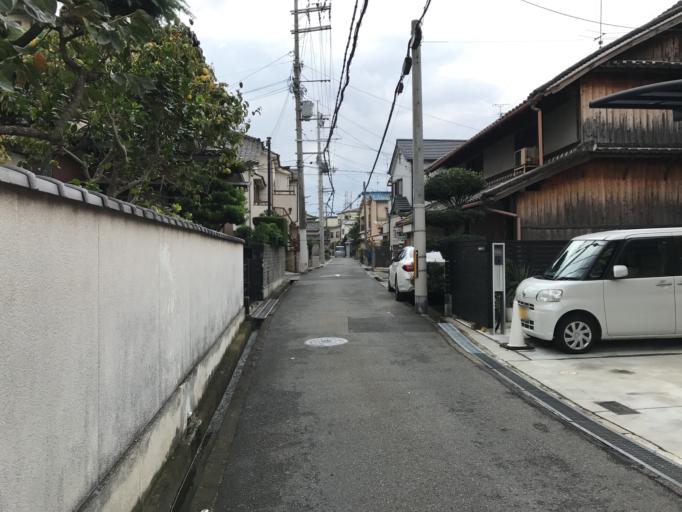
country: JP
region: Osaka
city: Kashihara
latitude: 34.5654
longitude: 135.6153
